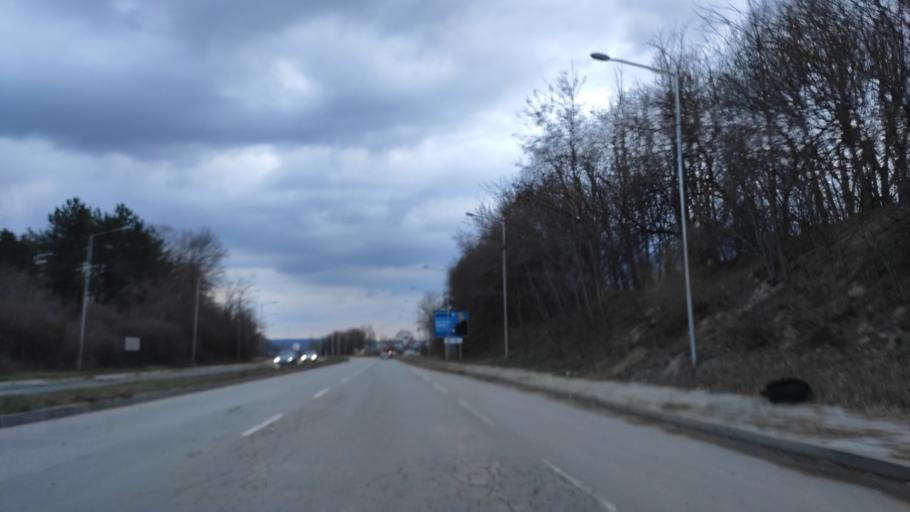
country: BG
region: Varna
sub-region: Obshtina Aksakovo
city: Aksakovo
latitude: 43.2276
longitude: 27.8602
